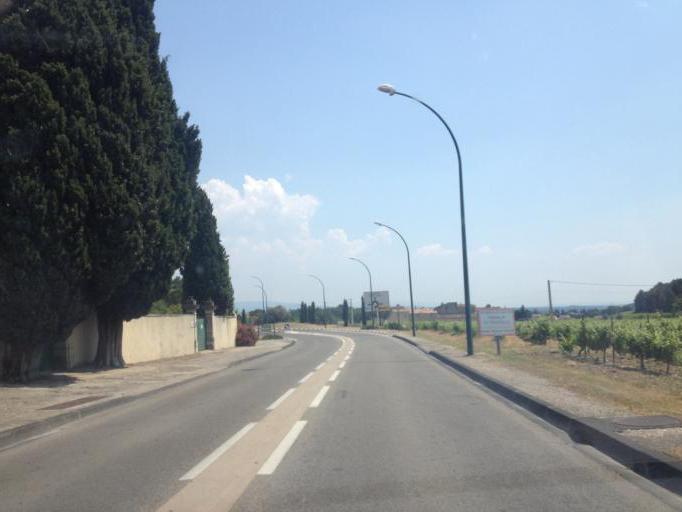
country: FR
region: Provence-Alpes-Cote d'Azur
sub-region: Departement du Vaucluse
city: Vacqueyras
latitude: 44.1341
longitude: 4.9873
